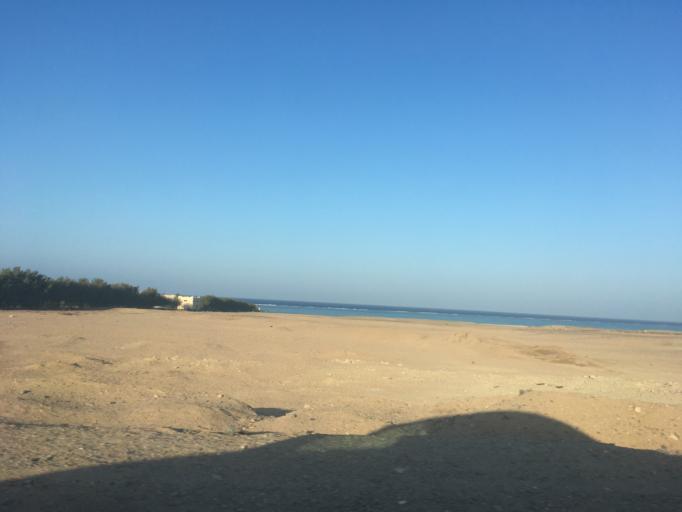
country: EG
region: Red Sea
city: Marsa Alam
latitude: 24.9177
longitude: 34.9626
